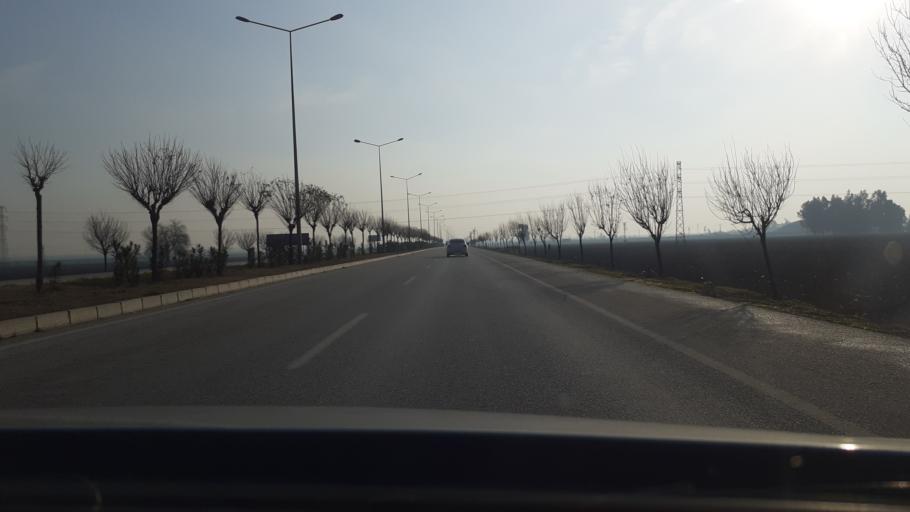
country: TR
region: Hatay
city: Serinyol
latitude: 36.3721
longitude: 36.2285
